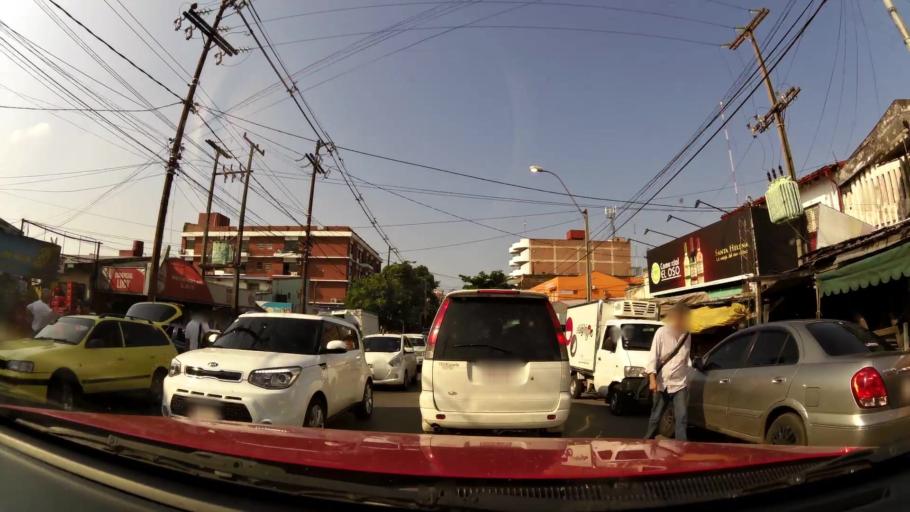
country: PY
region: Asuncion
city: Asuncion
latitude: -25.2978
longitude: -57.6254
